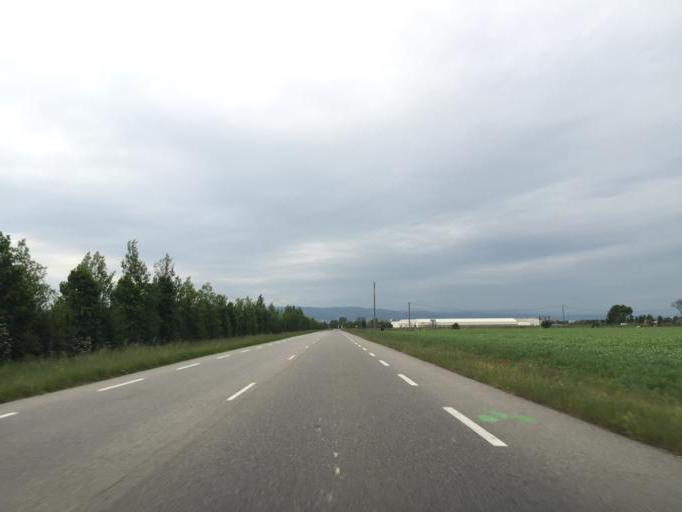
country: FR
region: Rhone-Alpes
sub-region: Departement de la Drome
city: Malissard
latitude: 44.9060
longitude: 4.9887
